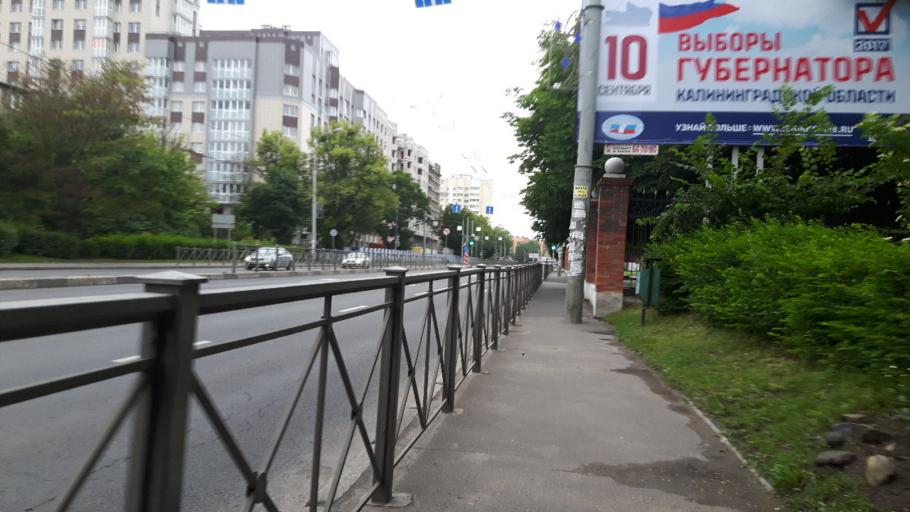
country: RU
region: Kaliningrad
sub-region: Gorod Kaliningrad
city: Kaliningrad
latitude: 54.7330
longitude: 20.4861
